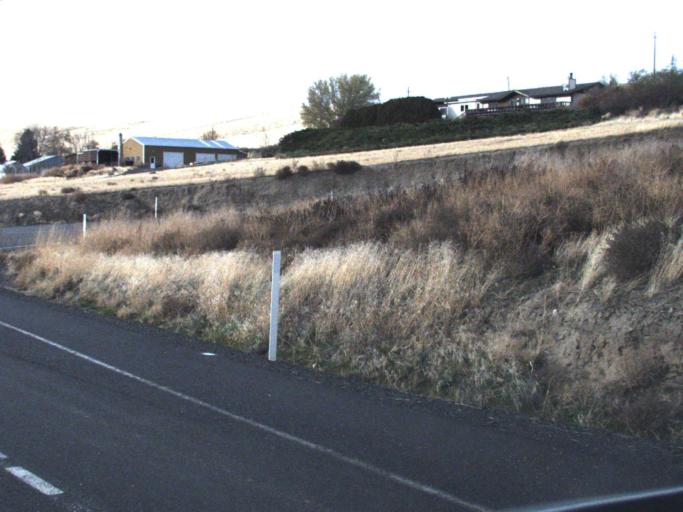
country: US
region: Washington
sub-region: Garfield County
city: Pomeroy
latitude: 46.4728
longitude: -117.5322
